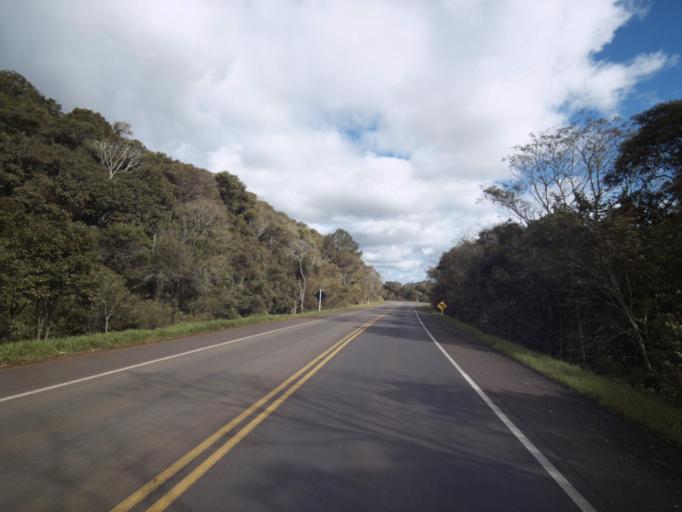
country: BR
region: Santa Catarina
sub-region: Concordia
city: Concordia
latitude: -27.3379
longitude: -51.9779
